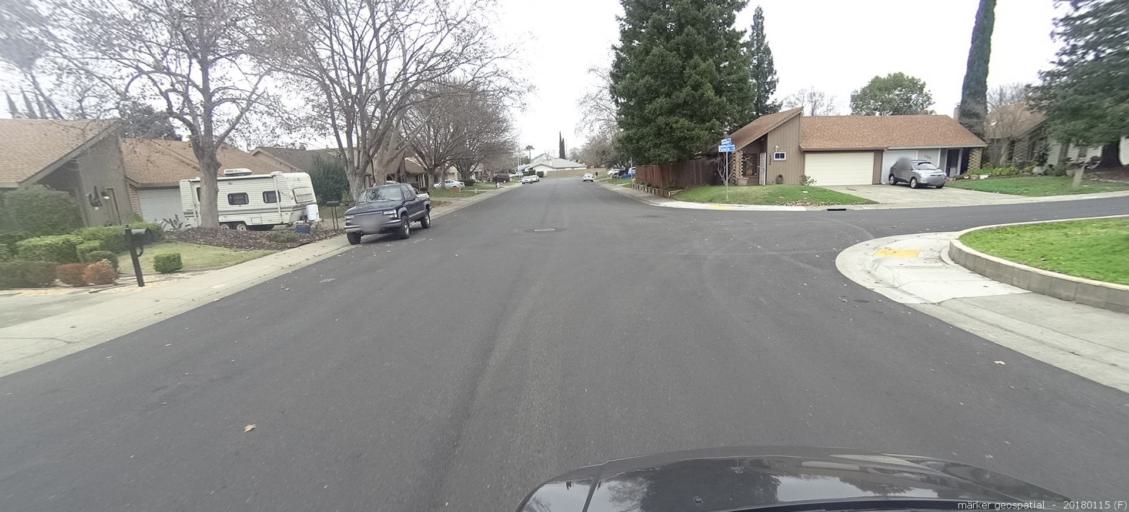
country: US
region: California
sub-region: Sacramento County
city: Rancho Cordova
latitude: 38.5921
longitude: -121.2905
